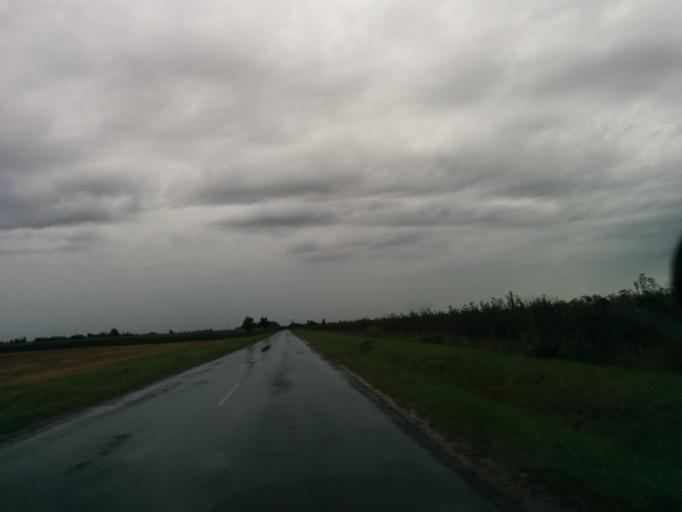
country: HU
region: Vas
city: Vep
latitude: 47.3064
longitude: 16.7073
